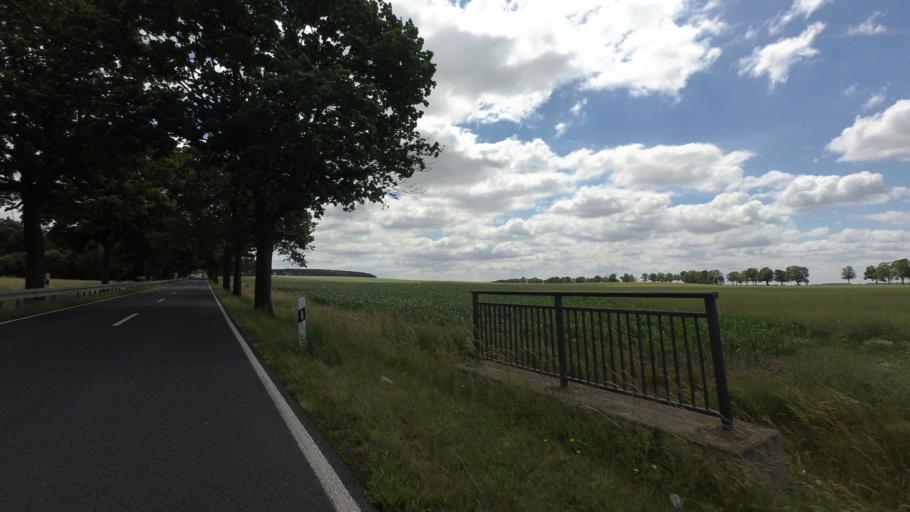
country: DE
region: Brandenburg
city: Juterbog
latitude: 51.9741
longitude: 13.1091
